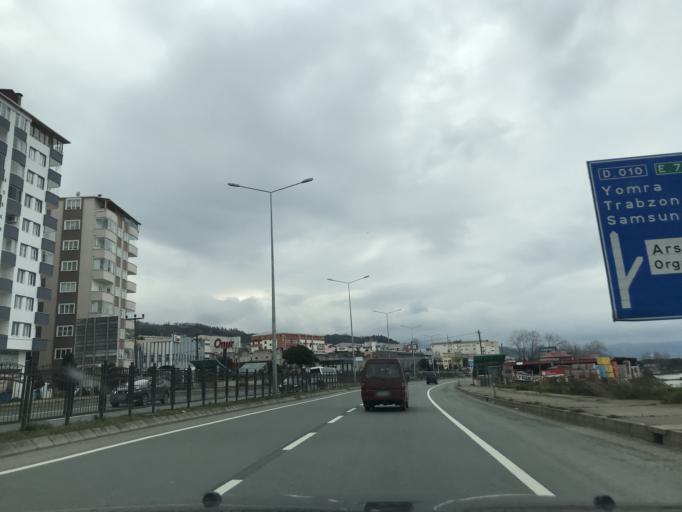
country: TR
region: Trabzon
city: Arsin
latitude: 40.9615
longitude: 39.9715
